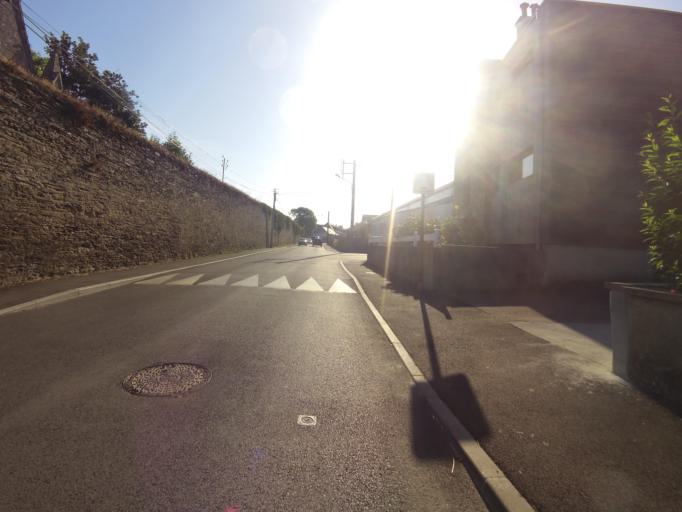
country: FR
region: Brittany
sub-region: Departement du Morbihan
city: Ploermel
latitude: 47.9293
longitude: -2.4034
